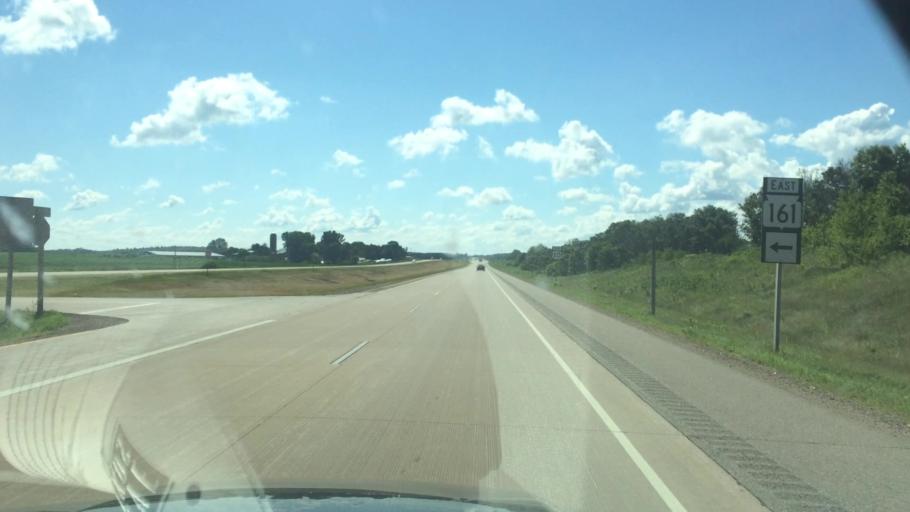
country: US
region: Wisconsin
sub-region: Portage County
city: Amherst
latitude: 44.4984
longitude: -89.3748
